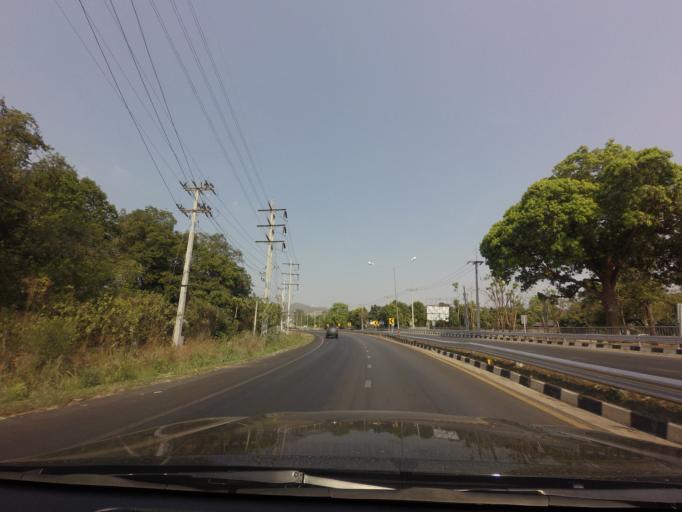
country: TH
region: Kanchanaburi
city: Kanchanaburi
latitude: 14.0607
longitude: 99.4843
